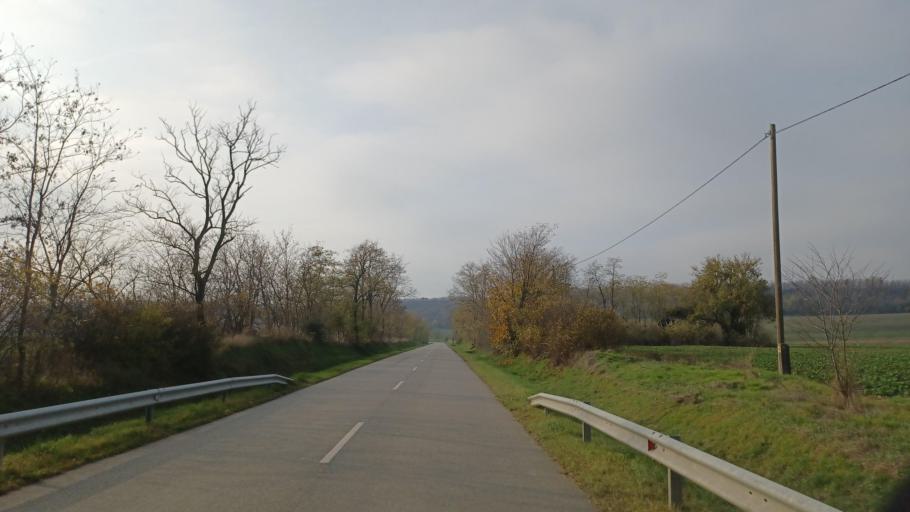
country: HU
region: Tolna
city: Dunaszentgyorgy
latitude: 46.5650
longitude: 18.7699
